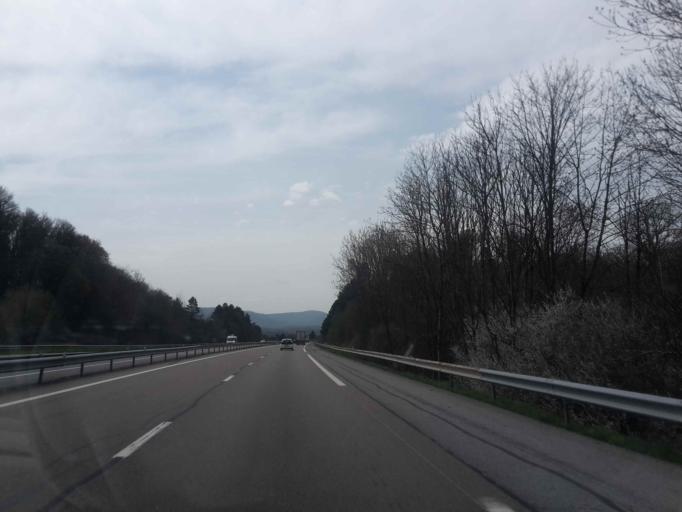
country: FR
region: Franche-Comte
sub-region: Departement du Doubs
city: Baume-les-Dames
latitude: 47.3636
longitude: 6.3247
